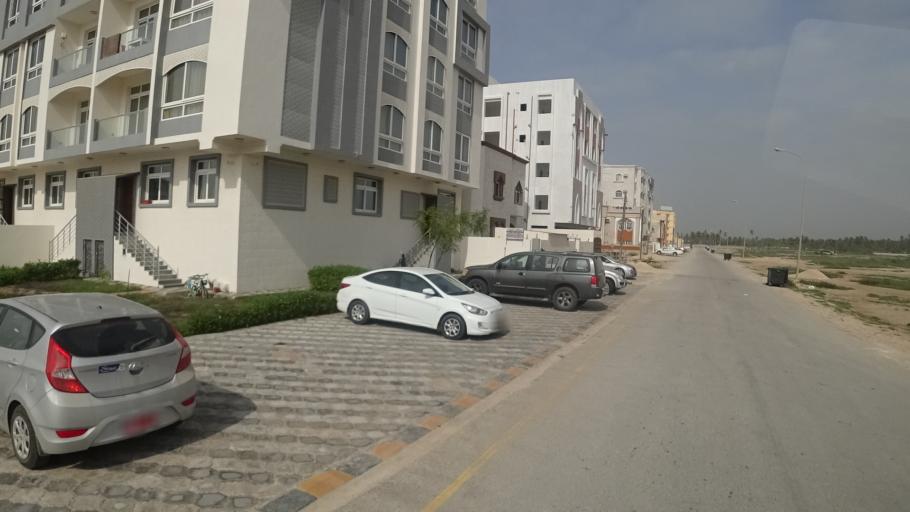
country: OM
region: Zufar
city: Salalah
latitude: 17.0164
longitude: 54.1746
